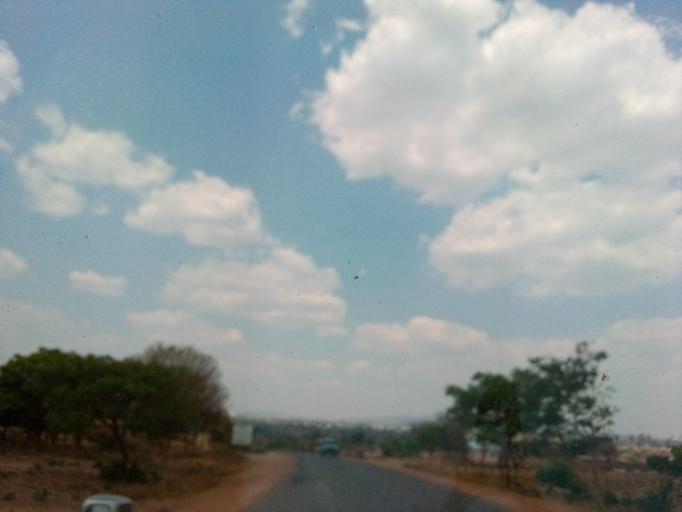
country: ZM
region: Northern
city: Mpika
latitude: -11.8362
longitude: 31.3868
